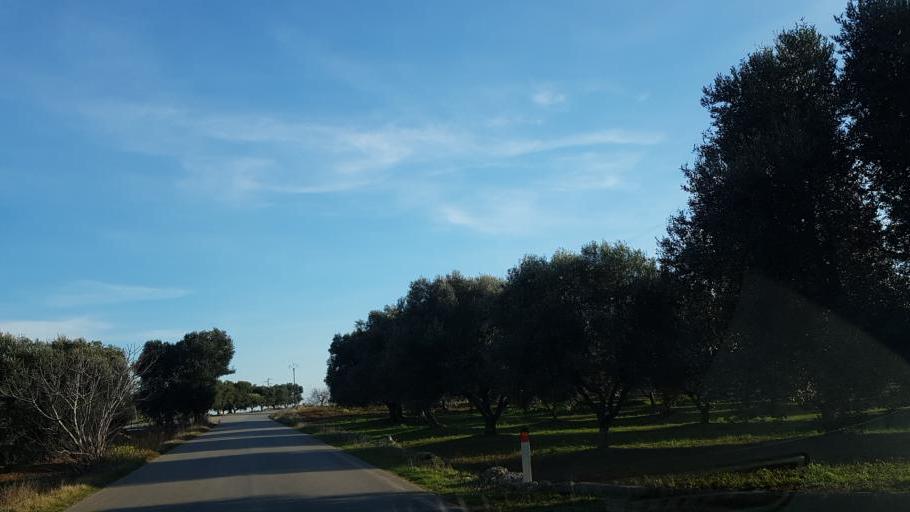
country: IT
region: Apulia
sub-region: Provincia di Brindisi
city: San Vito dei Normanni
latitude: 40.6903
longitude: 17.7633
